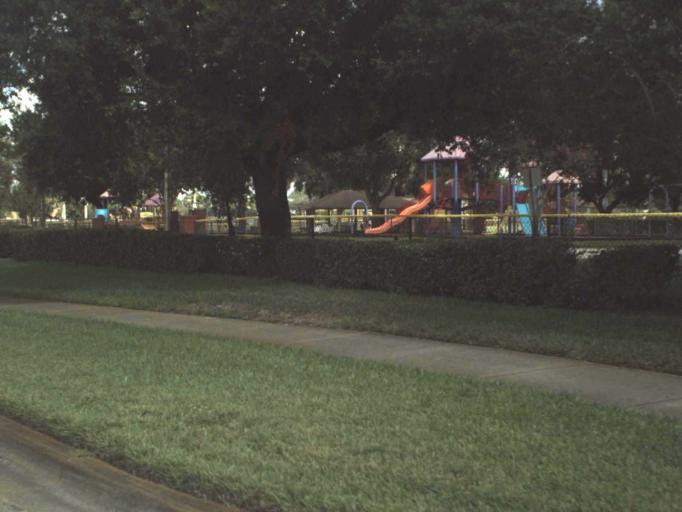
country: US
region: Florida
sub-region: Saint Lucie County
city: River Park
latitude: 27.3177
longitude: -80.3510
